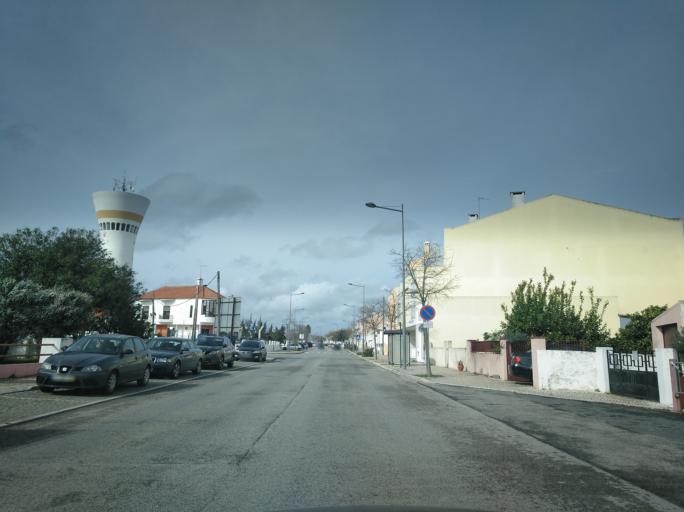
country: PT
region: Setubal
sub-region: Grandola
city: Grandola
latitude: 38.1814
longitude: -8.5671
